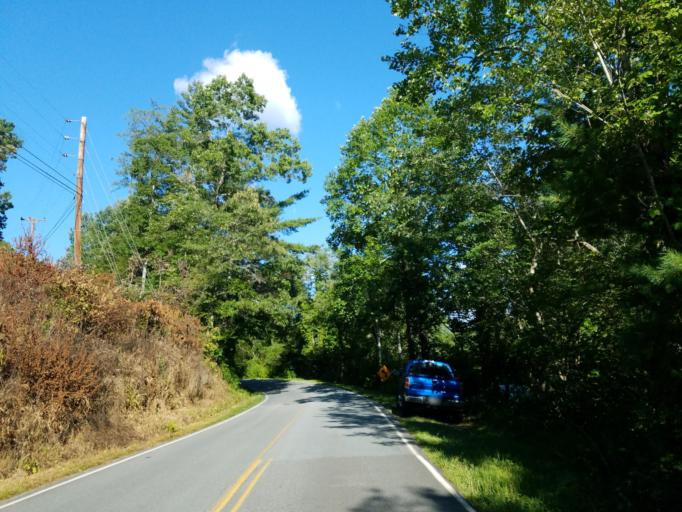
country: US
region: Georgia
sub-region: Fannin County
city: Blue Ridge
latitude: 34.7578
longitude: -84.1995
